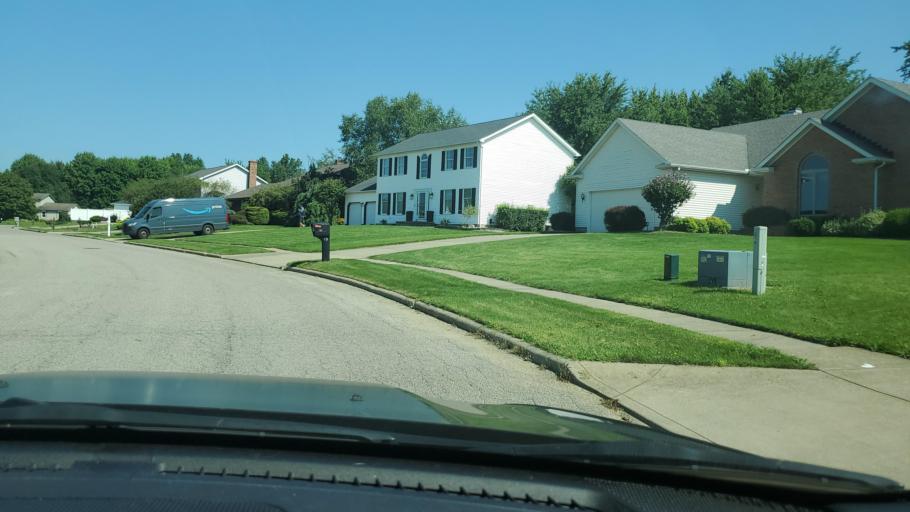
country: US
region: Ohio
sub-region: Trumbull County
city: Girard
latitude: 41.1752
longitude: -80.6934
